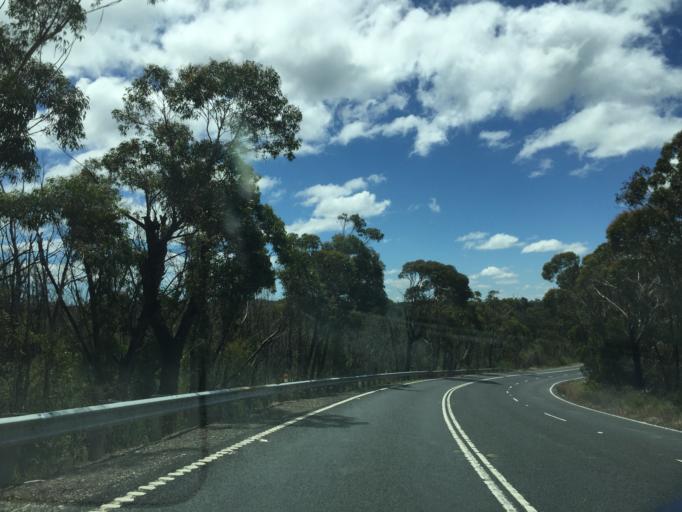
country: AU
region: New South Wales
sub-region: Blue Mountains Municipality
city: Blackheath
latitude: -33.5609
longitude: 150.3432
